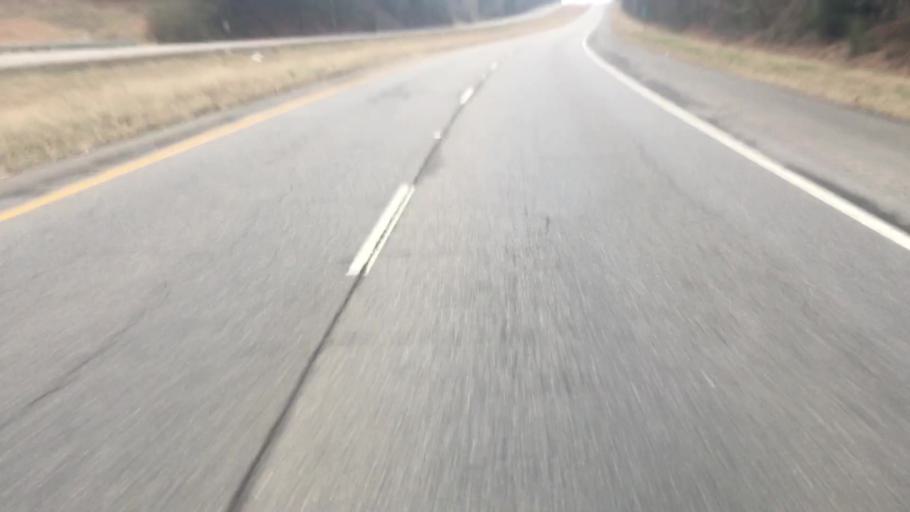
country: US
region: Alabama
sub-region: Walker County
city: Sumiton
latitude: 33.7719
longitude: -87.0729
